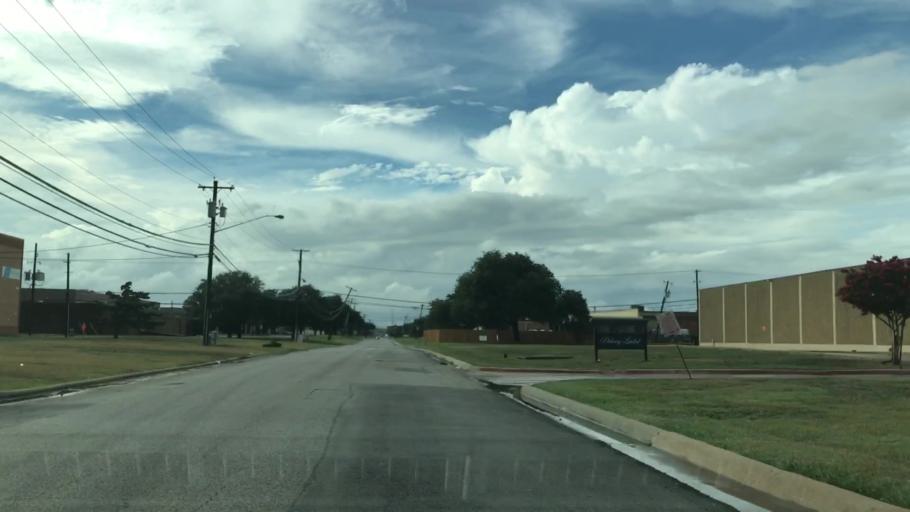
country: US
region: Texas
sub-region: Dallas County
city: Irving
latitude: 32.8194
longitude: -96.8790
